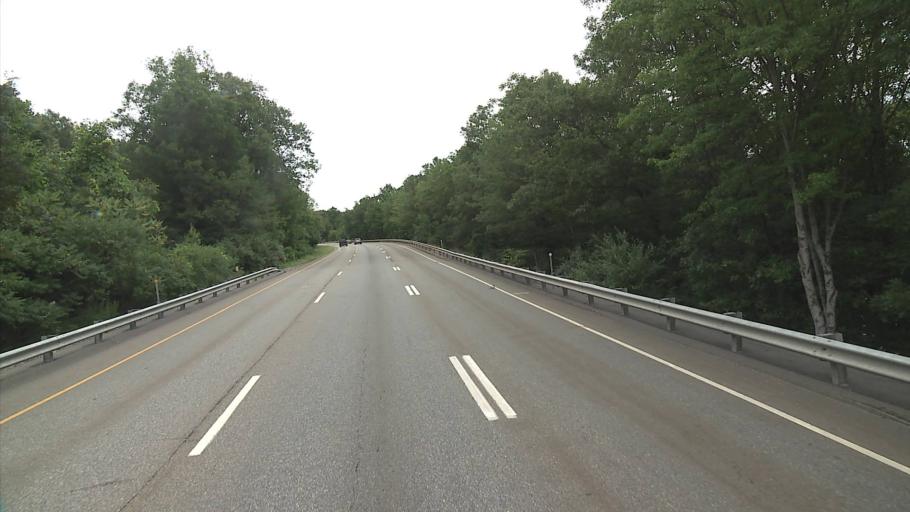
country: US
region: Connecticut
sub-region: Litchfield County
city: Thomaston
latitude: 41.6927
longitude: -73.0688
